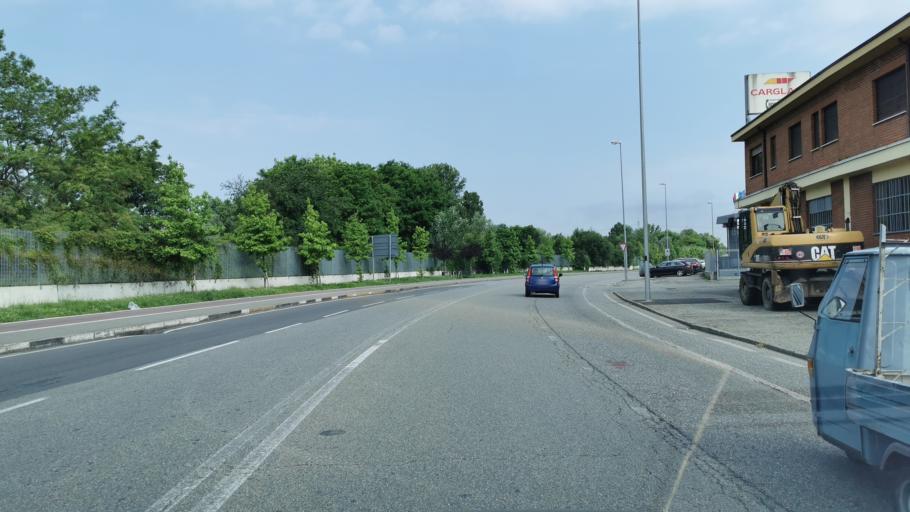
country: IT
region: Piedmont
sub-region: Provincia di Torino
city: Turin
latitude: 45.0996
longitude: 7.7221
